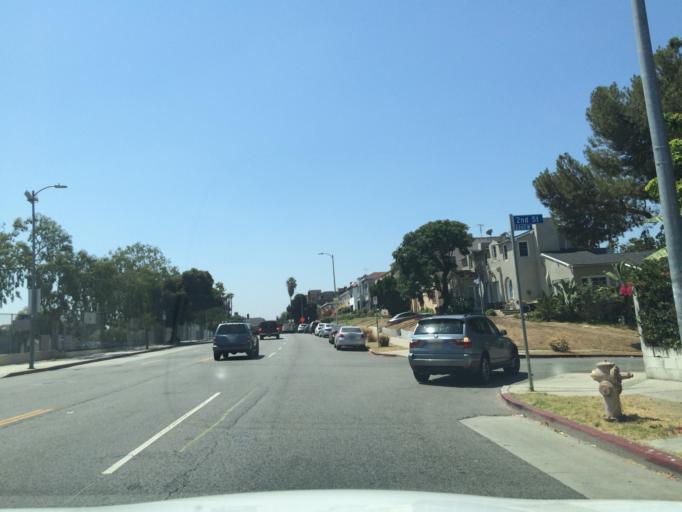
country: US
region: California
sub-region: Los Angeles County
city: Silver Lake
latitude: 34.0708
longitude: -118.2868
